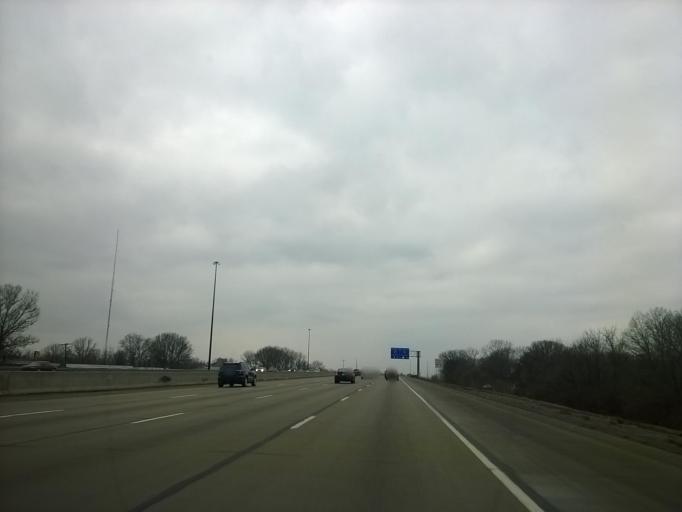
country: US
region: Indiana
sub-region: Marion County
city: Warren Park
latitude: 39.8045
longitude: -86.0713
